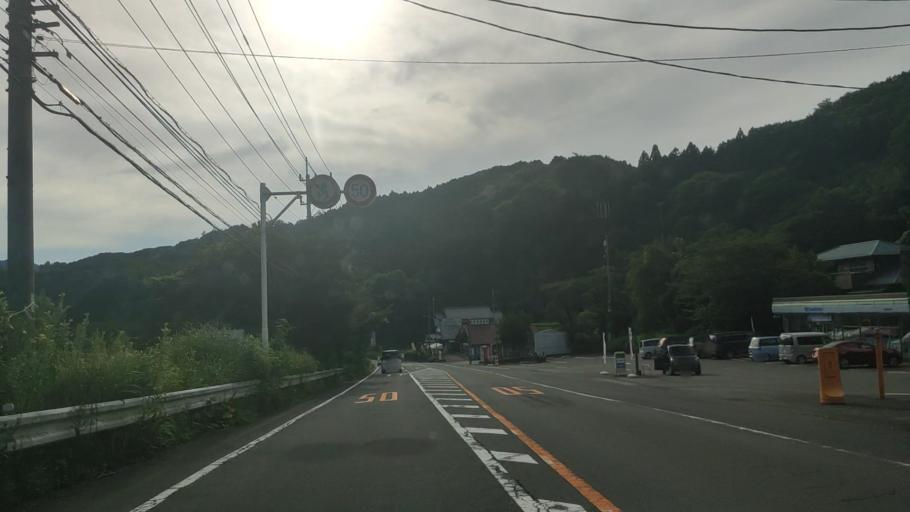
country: JP
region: Gunma
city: Omamacho-omama
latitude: 36.4910
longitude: 139.2728
